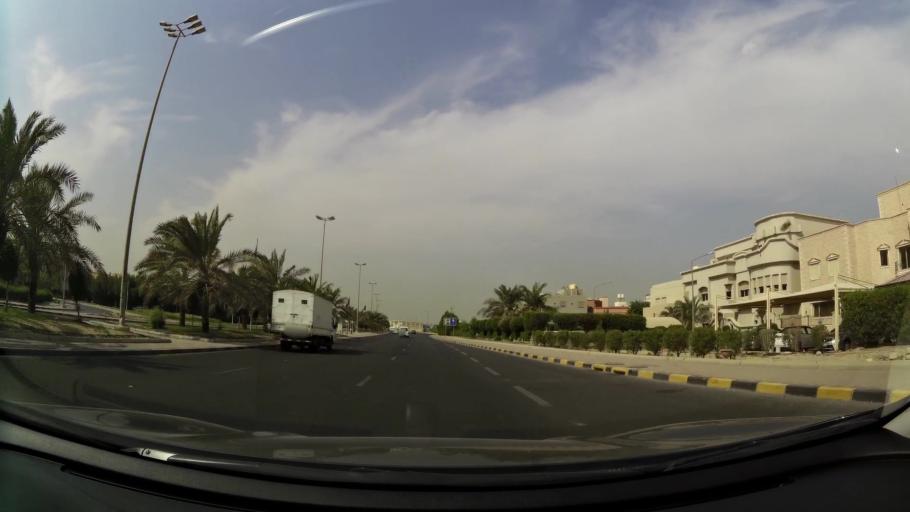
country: KW
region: Al Farwaniyah
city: Janub as Surrah
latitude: 29.2829
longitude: 48.0094
